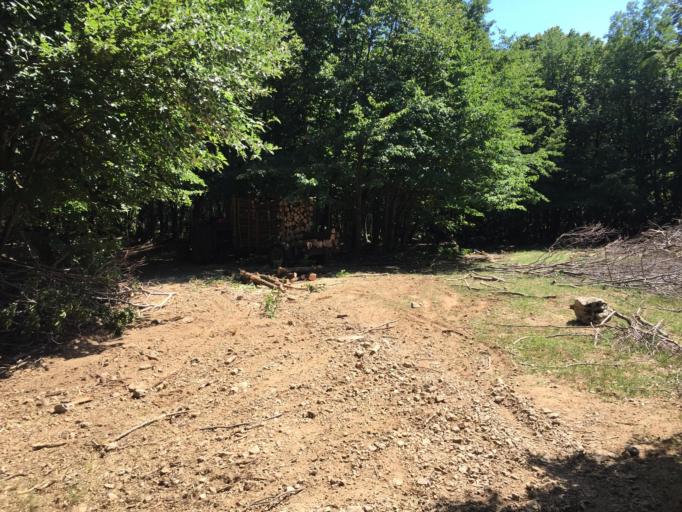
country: HR
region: Primorsko-Goranska
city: Drazice
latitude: 45.4494
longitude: 14.4547
